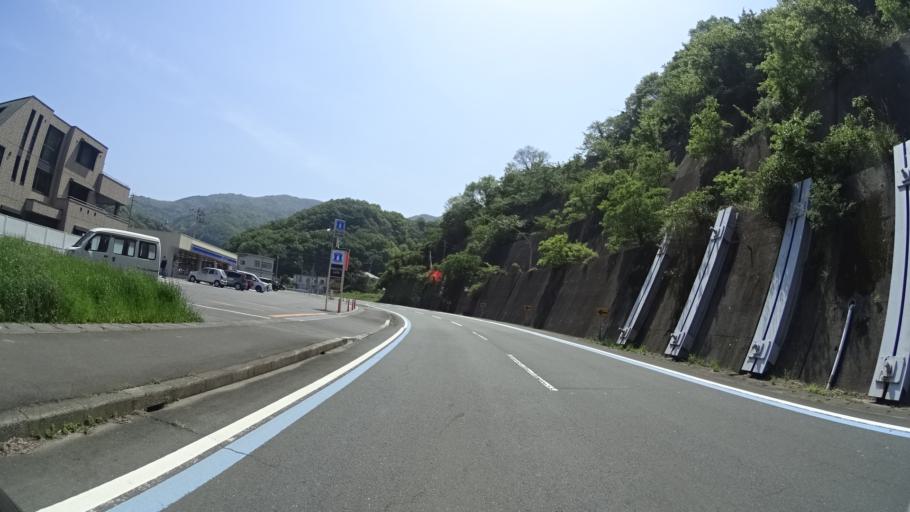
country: JP
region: Ehime
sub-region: Nishiuwa-gun
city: Ikata-cho
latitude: 33.3865
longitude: 132.1254
